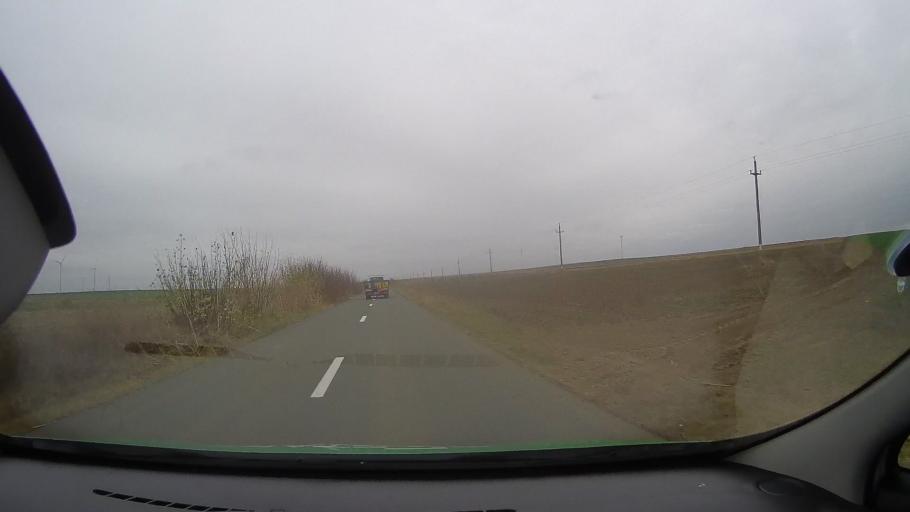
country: RO
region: Constanta
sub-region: Comuna Targusor
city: Targusor
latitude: 44.4675
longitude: 28.3924
